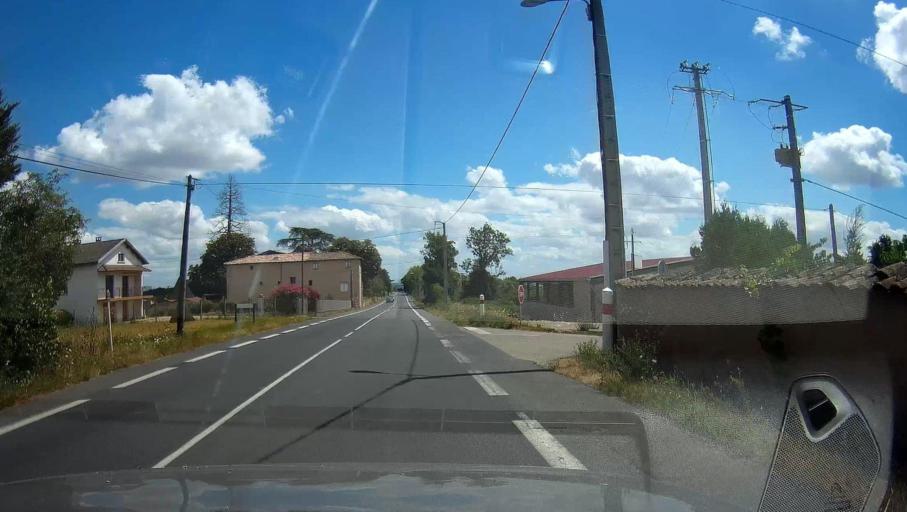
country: FR
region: Rhone-Alpes
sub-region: Departement du Rhone
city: Gleize
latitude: 45.9941
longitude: 4.6795
